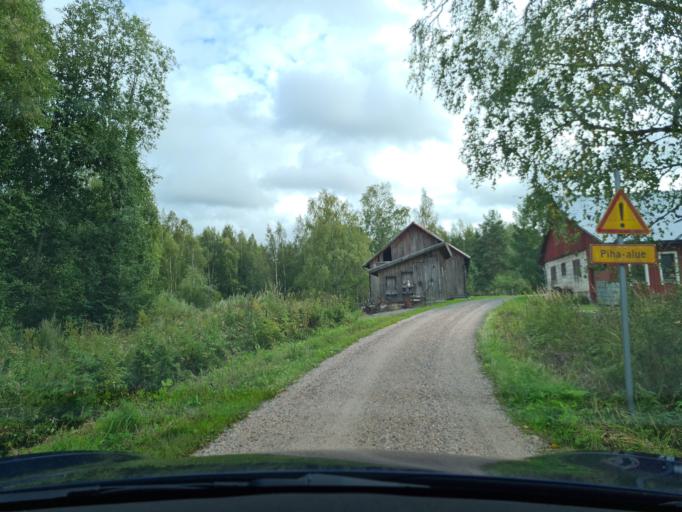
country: FI
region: Uusimaa
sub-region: Helsinki
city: Vihti
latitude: 60.4124
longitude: 24.4936
